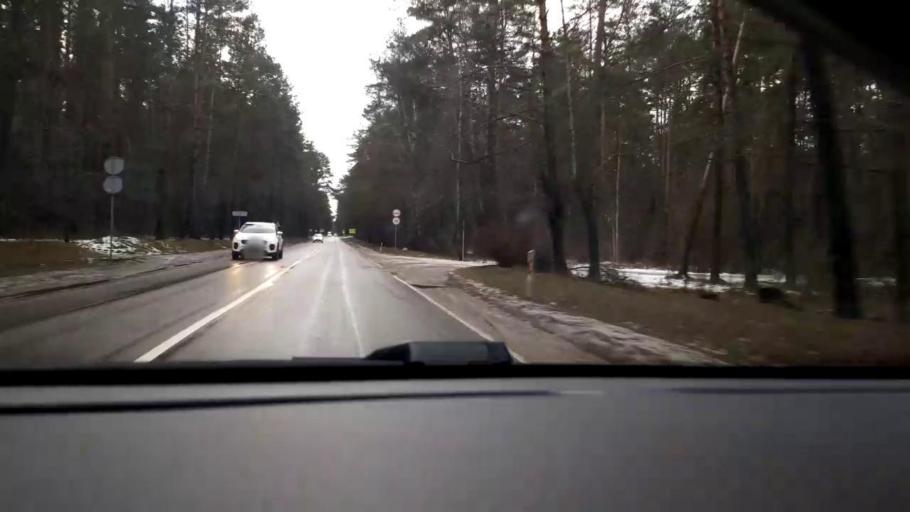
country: LT
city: Nemencine
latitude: 54.7856
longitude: 25.3836
